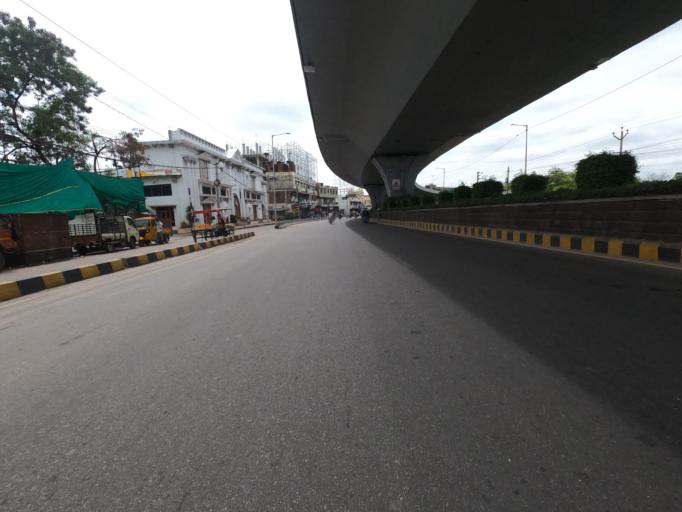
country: IN
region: Telangana
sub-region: Hyderabad
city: Hyderabad
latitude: 17.3421
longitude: 78.4222
